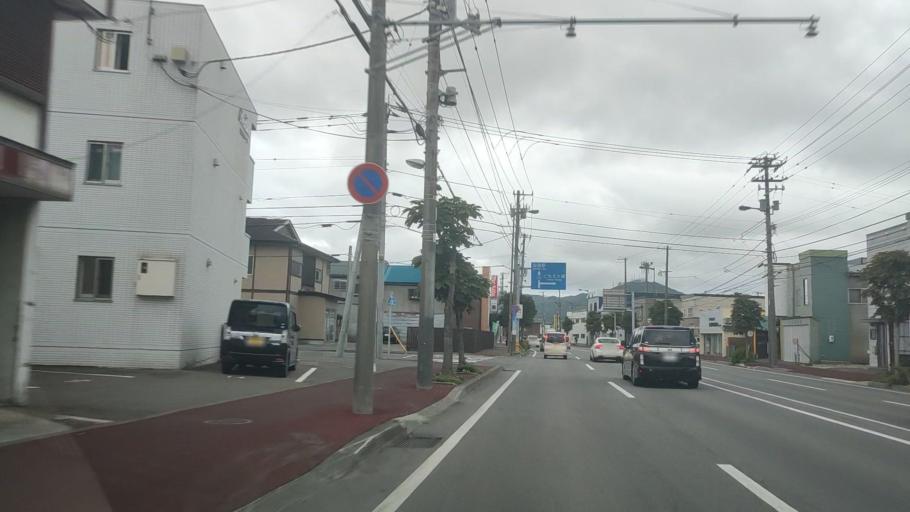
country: JP
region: Hokkaido
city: Hakodate
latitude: 41.7880
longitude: 140.7315
